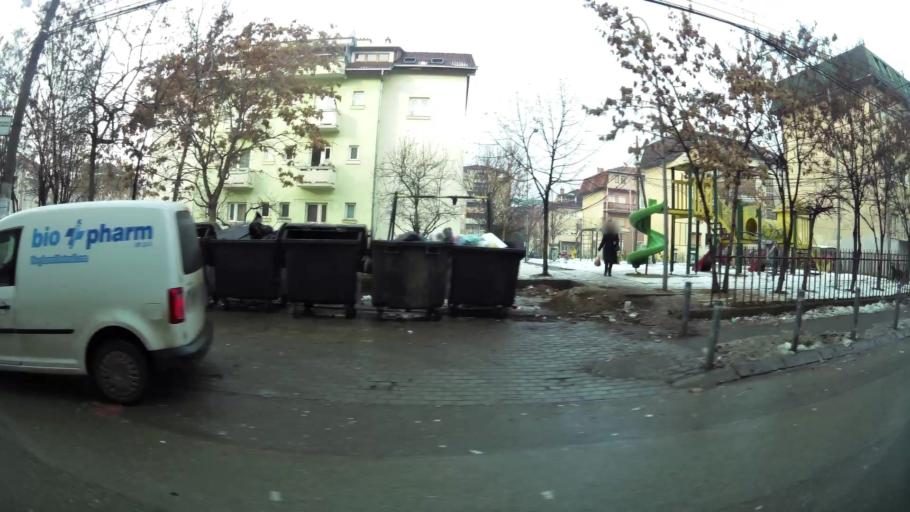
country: XK
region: Pristina
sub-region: Komuna e Prishtines
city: Pristina
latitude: 42.6672
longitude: 21.1707
